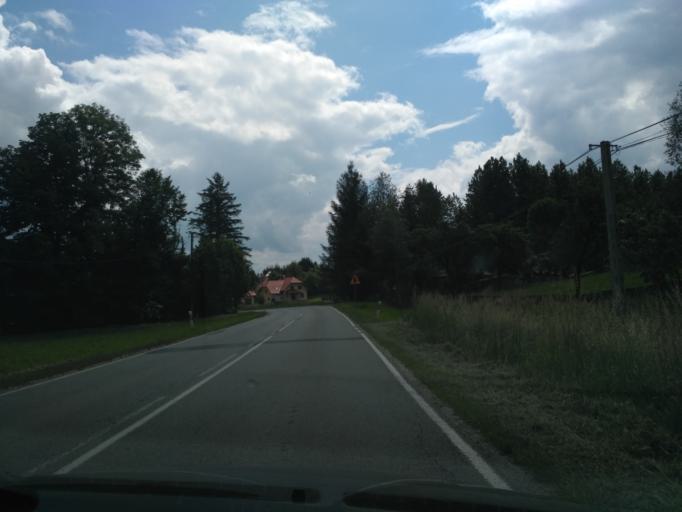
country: PL
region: Subcarpathian Voivodeship
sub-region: Powiat rzeszowski
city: Blazowa
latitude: 49.9270
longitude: 22.1249
